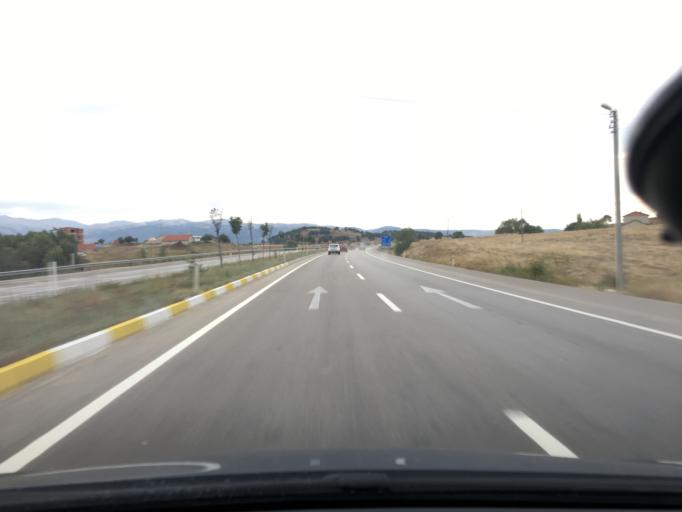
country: TR
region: Afyonkarahisar
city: Sincanli
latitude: 38.6599
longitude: 30.3231
